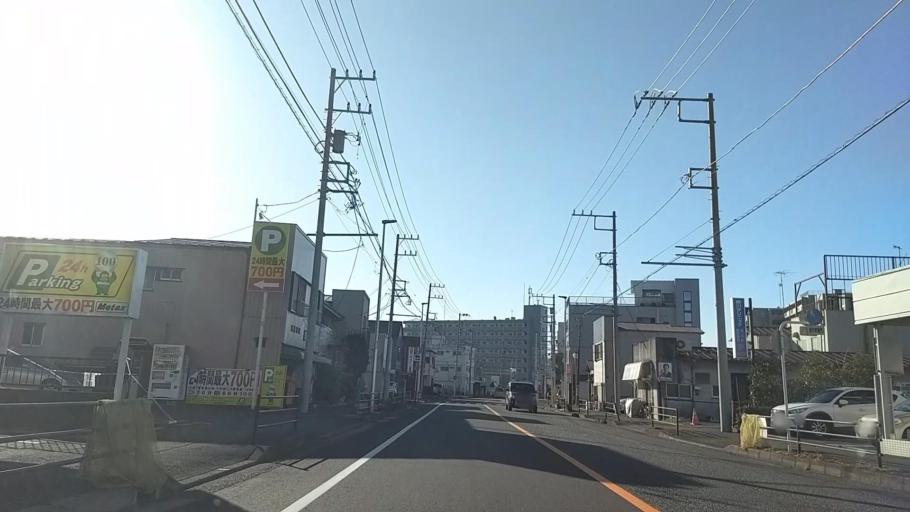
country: JP
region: Kanagawa
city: Atsugi
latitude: 35.4402
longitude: 139.3707
